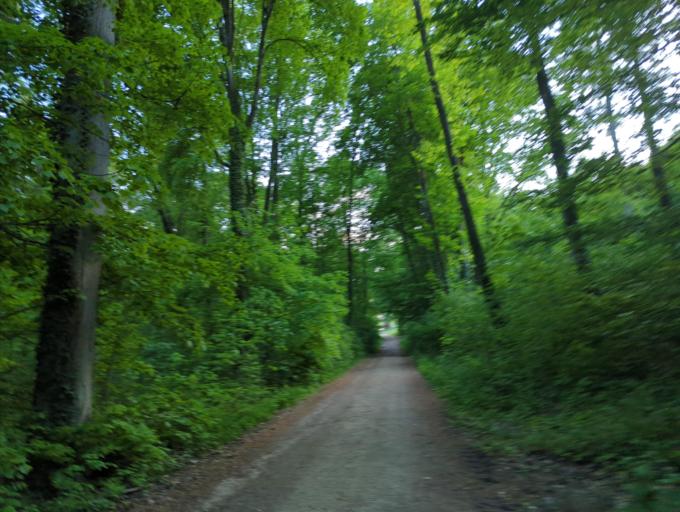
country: DE
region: Bavaria
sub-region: Upper Palatinate
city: Alteglofsheim
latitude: 48.9027
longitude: 12.1851
